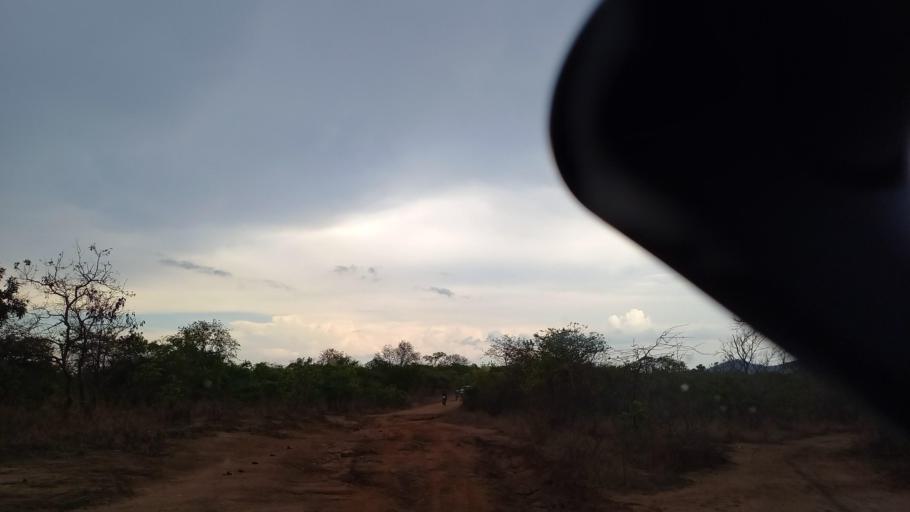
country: ZM
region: Lusaka
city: Kafue
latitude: -16.0001
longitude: 28.2797
